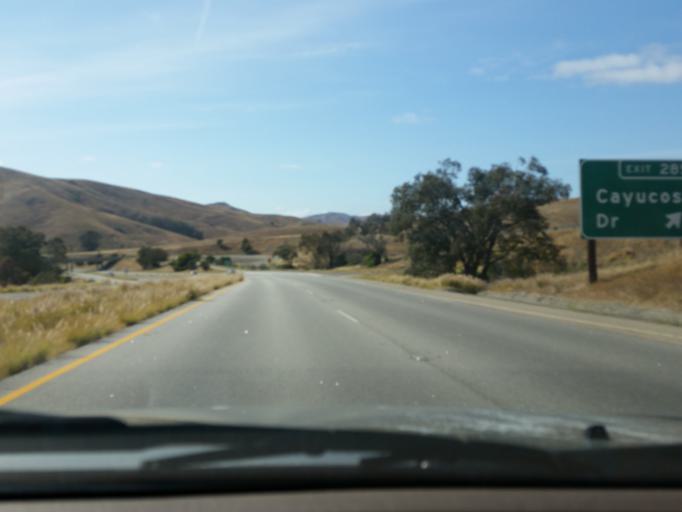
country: US
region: California
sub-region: San Luis Obispo County
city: Cayucos
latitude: 35.4509
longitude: -120.8997
